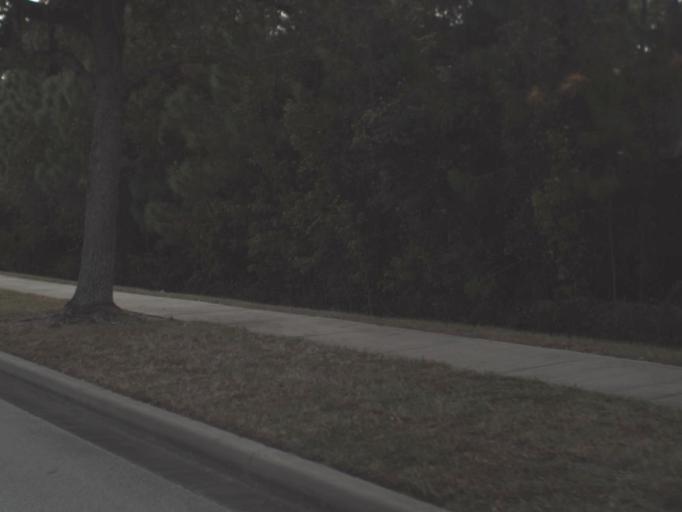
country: US
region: Florida
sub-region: Orange County
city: Taft
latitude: 28.4061
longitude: -81.2441
